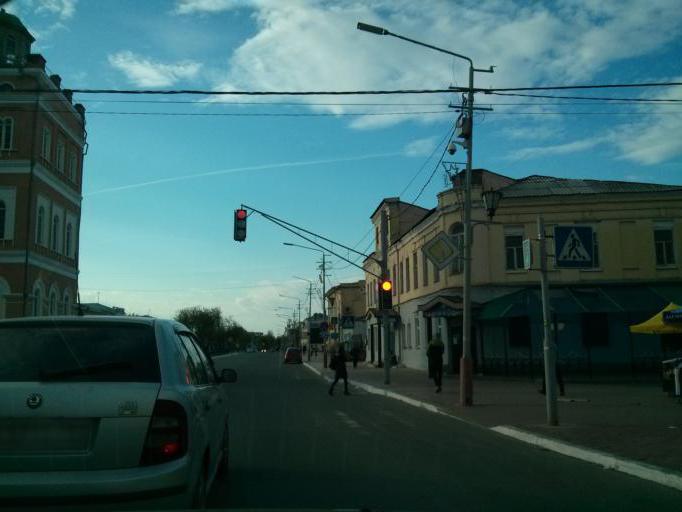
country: RU
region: Vladimir
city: Murom
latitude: 55.5778
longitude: 42.0535
